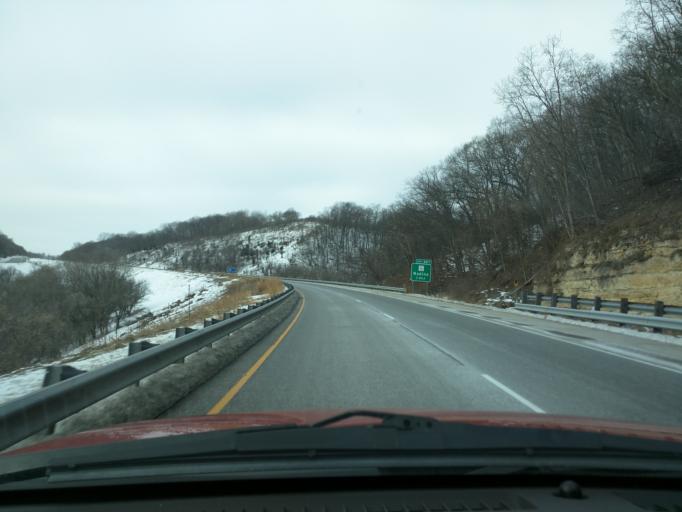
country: US
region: Wisconsin
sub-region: Trempealeau County
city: Trempealeau
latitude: 43.9339
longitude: -91.4165
